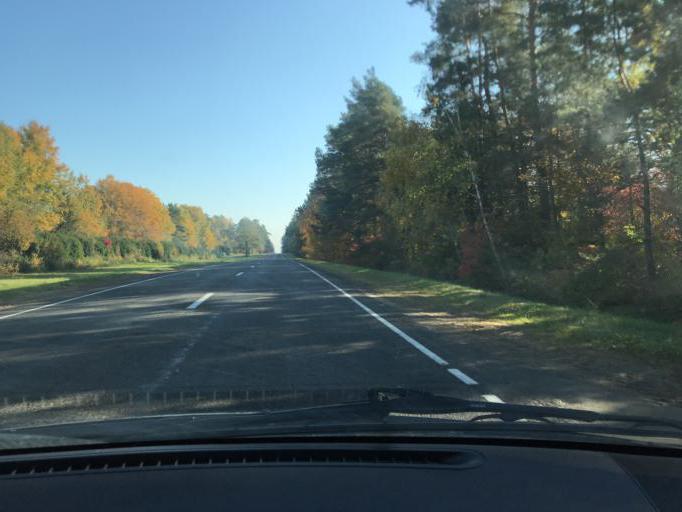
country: BY
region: Brest
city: Lyakhavichy
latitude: 52.9555
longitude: 26.2854
